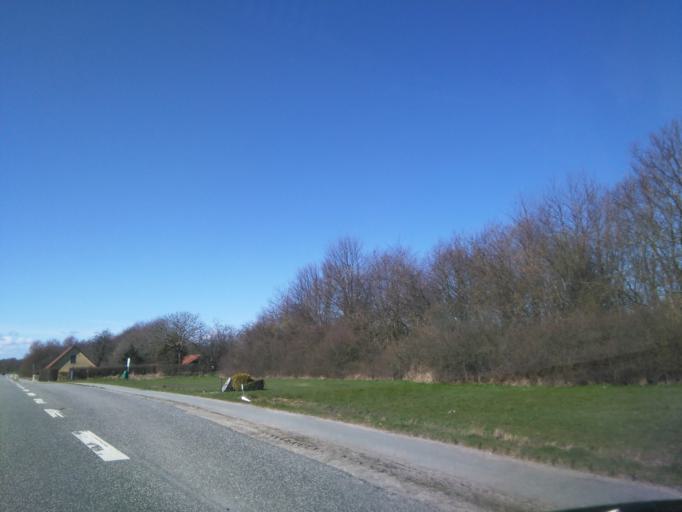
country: DK
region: Central Jutland
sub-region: Arhus Kommune
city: Kolt
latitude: 56.1041
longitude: 10.0847
